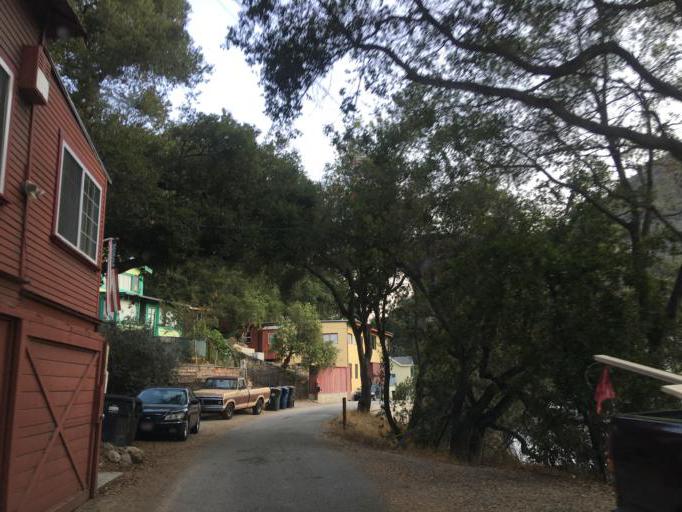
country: US
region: California
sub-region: Los Angeles County
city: Topanga
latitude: 34.0826
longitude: -118.5990
